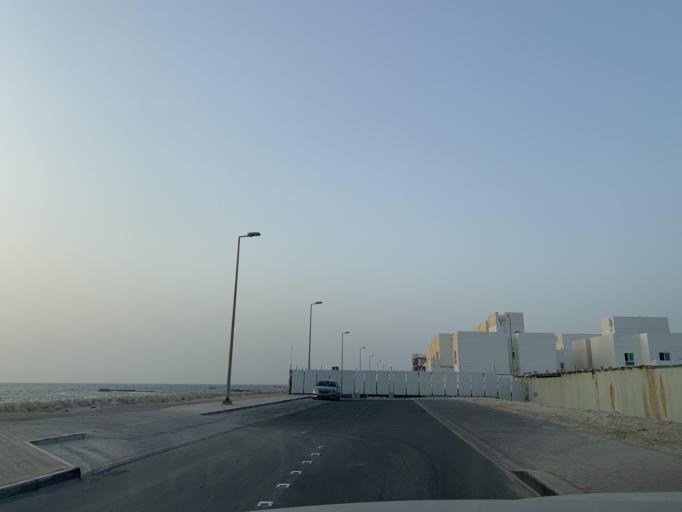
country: BH
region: Manama
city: Jidd Hafs
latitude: 26.2238
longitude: 50.4384
